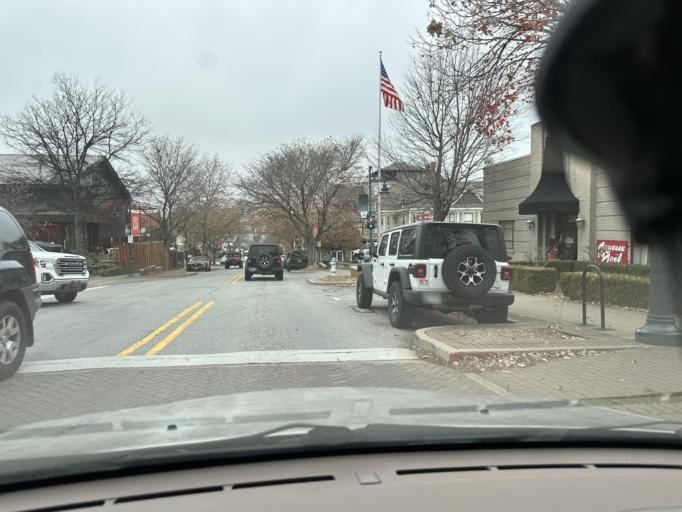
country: US
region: Arkansas
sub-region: Washington County
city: Fayetteville
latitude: 36.0664
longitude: -94.1615
